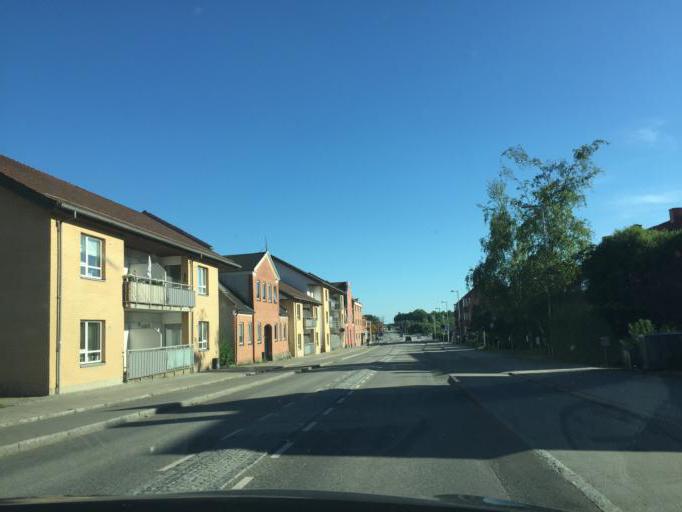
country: DK
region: Zealand
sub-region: Ringsted Kommune
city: Ringsted
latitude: 55.4410
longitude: 11.7931
